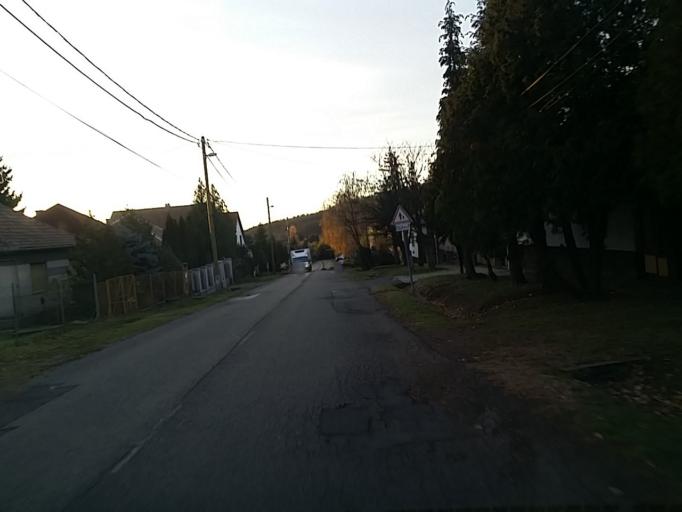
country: HU
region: Heves
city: Gyongyossolymos
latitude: 47.8259
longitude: 19.9724
